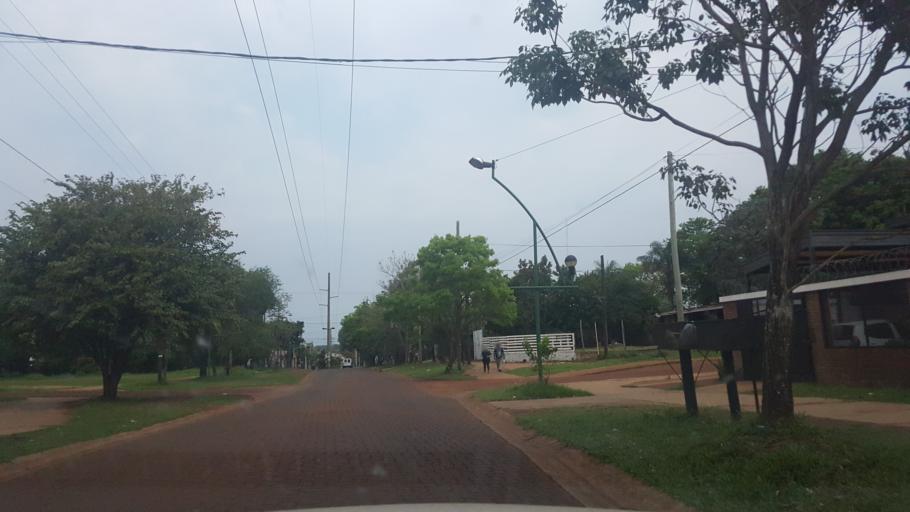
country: AR
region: Misiones
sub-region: Departamento de Capital
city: Posadas
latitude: -27.3979
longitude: -55.9170
